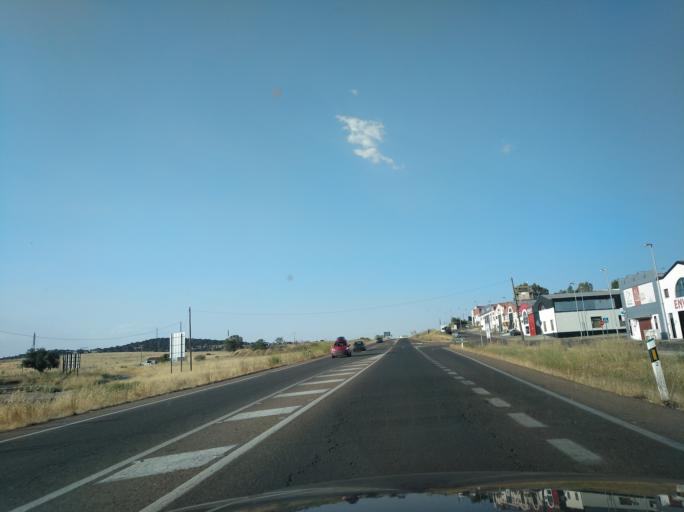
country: ES
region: Extremadura
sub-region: Provincia de Badajoz
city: Olivenza
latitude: 38.6951
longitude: -7.0909
